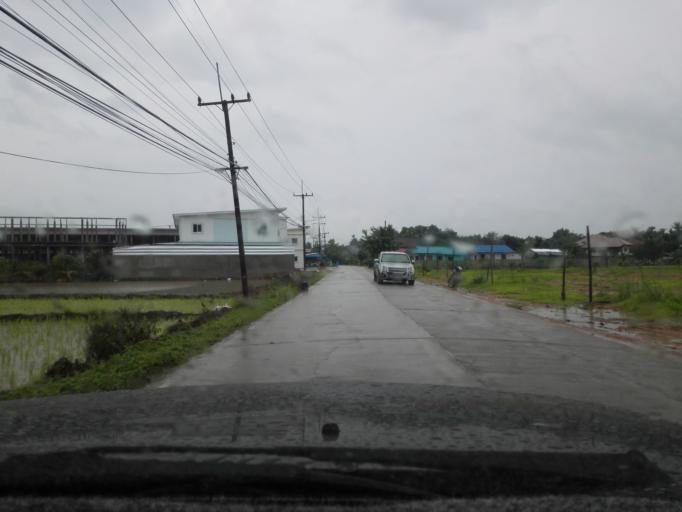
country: TH
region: Tak
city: Mae Sot
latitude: 16.6831
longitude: 98.5773
